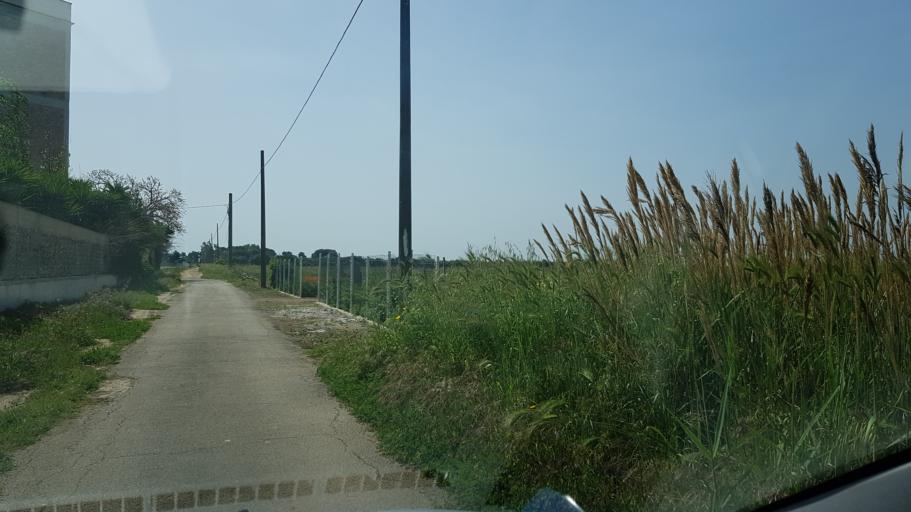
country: IT
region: Apulia
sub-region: Provincia di Brindisi
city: Materdomini
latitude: 40.6746
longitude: 17.9340
